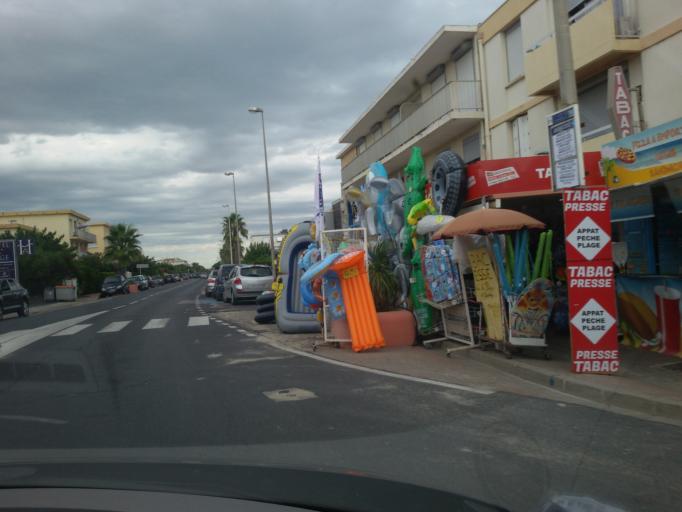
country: FR
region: Languedoc-Roussillon
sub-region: Departement de l'Herault
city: Palavas-les-Flots
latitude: 43.5330
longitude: 3.9485
